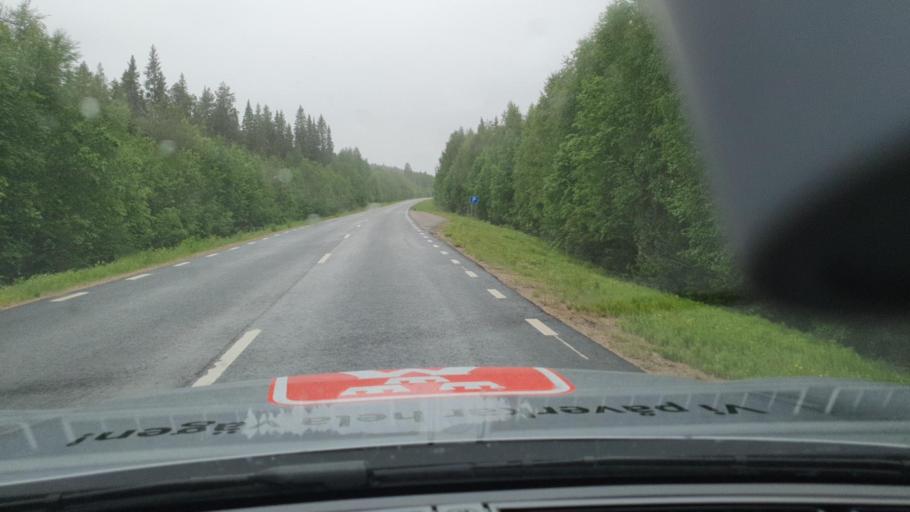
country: SE
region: Norrbotten
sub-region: Overtornea Kommun
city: OEvertornea
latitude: 66.4394
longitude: 23.3221
